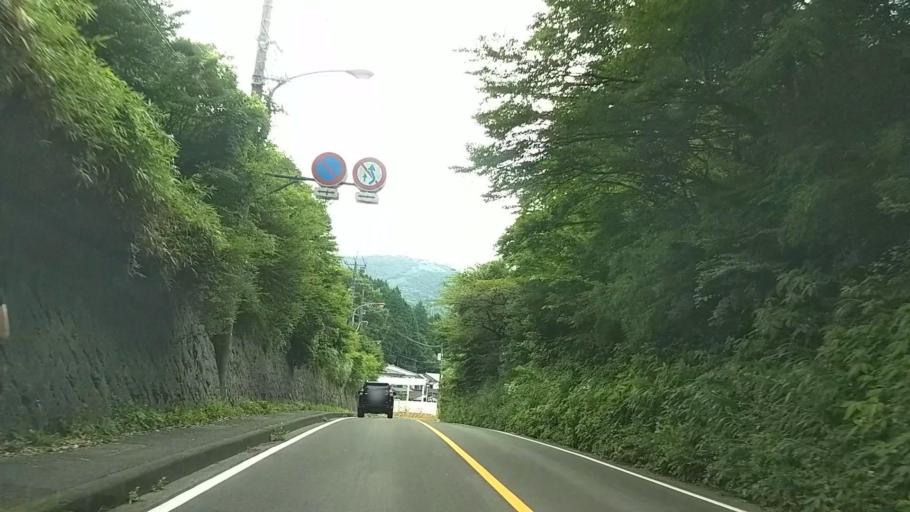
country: JP
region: Kanagawa
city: Hakone
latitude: 35.1926
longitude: 139.0272
